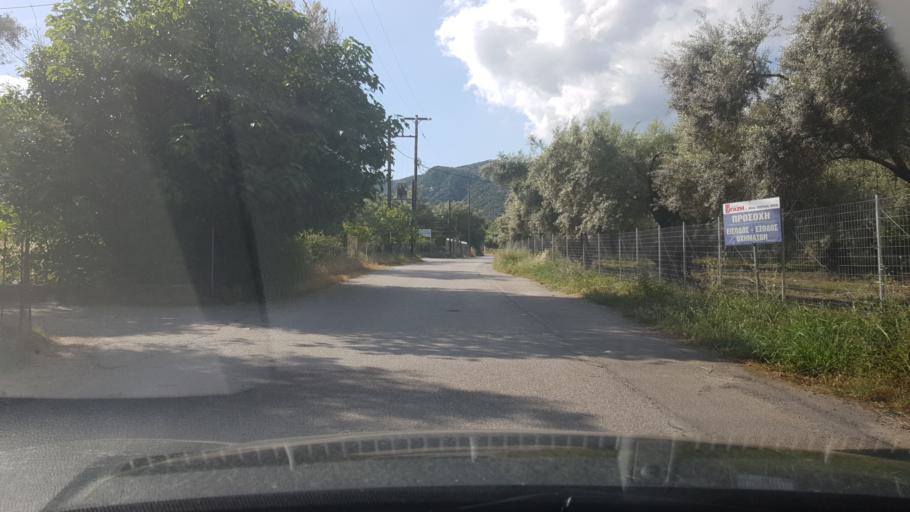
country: GR
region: Ionian Islands
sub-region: Lefkada
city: Nidri
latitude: 38.7123
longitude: 20.7035
